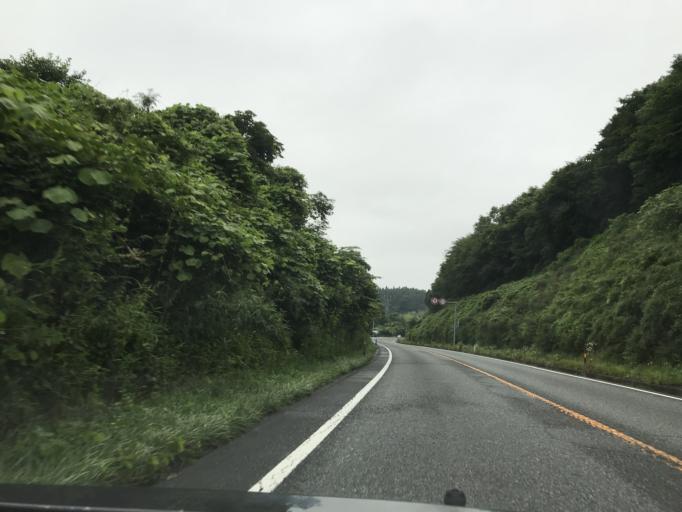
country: JP
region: Iwate
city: Ichinoseki
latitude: 38.8971
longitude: 141.1148
